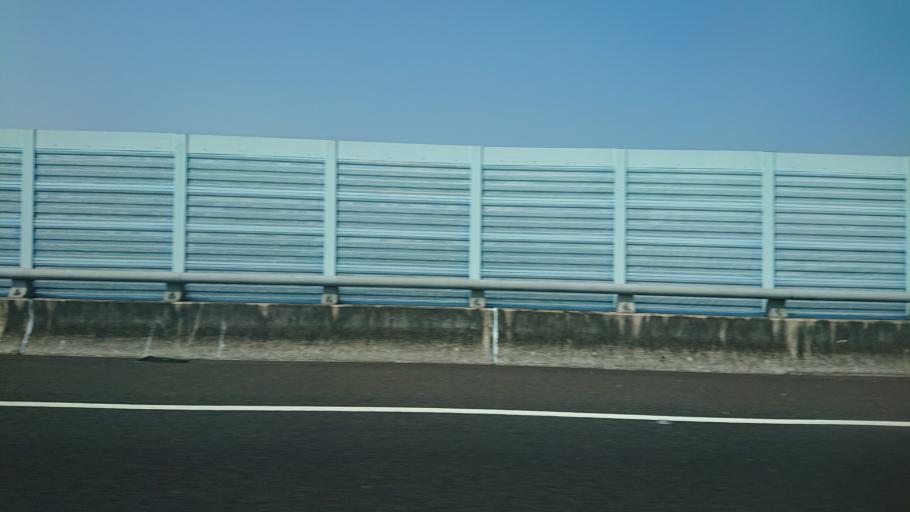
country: TW
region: Taiwan
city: Lugu
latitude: 23.8286
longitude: 120.7083
